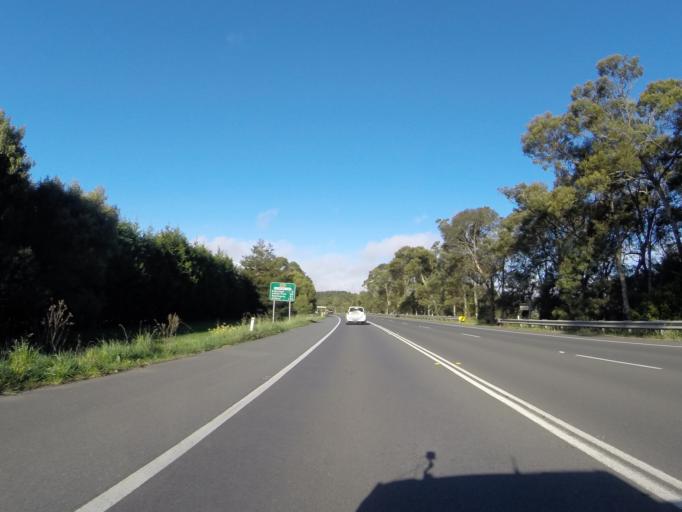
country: AU
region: New South Wales
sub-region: Shellharbour
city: Calderwood
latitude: -34.5898
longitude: 150.5707
